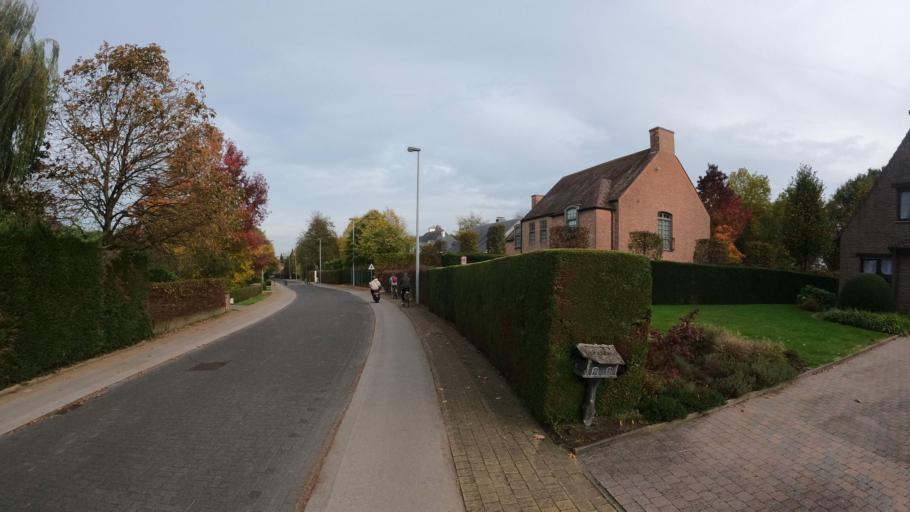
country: BE
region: Flanders
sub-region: Provincie Oost-Vlaanderen
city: Sint-Niklaas
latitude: 51.1516
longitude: 4.1651
